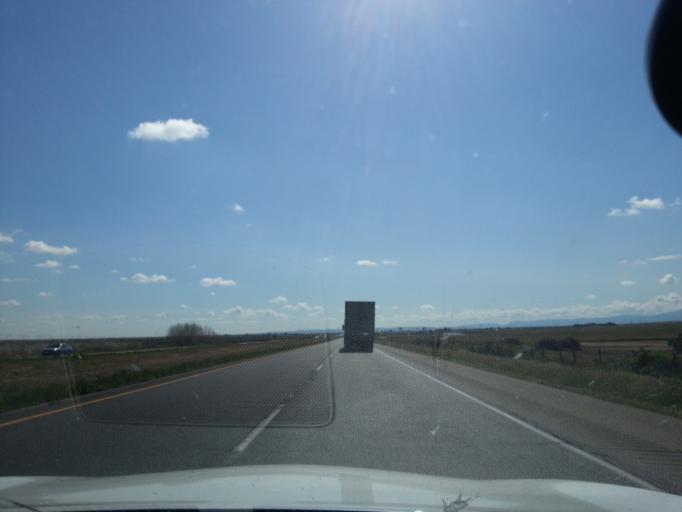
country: US
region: California
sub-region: Fresno County
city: Coalinga
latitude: 36.2772
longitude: -120.2587
